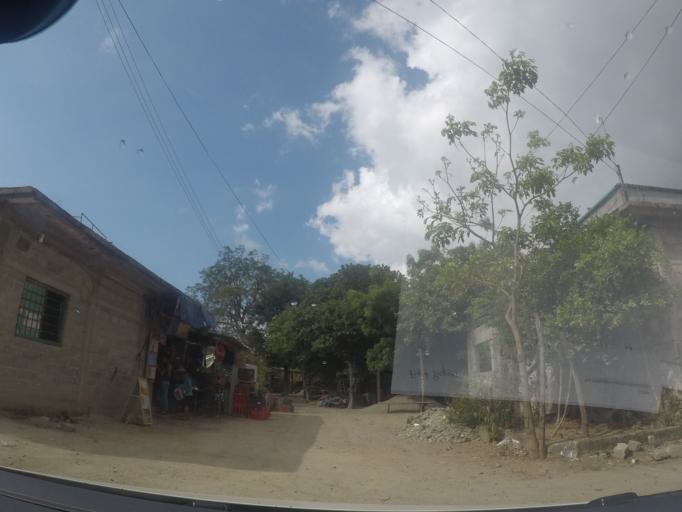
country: MX
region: Oaxaca
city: Juchitan de Zaragoza
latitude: 16.4293
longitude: -95.0304
